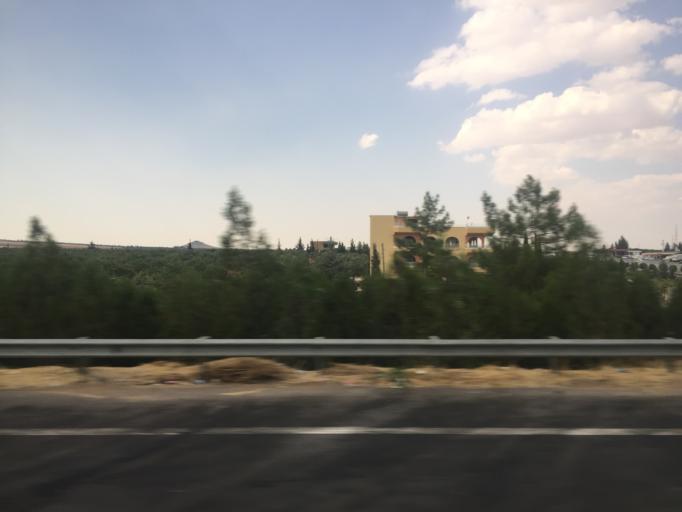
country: TR
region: Sanliurfa
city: Akziyaret
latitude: 37.2693
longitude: 38.7941
